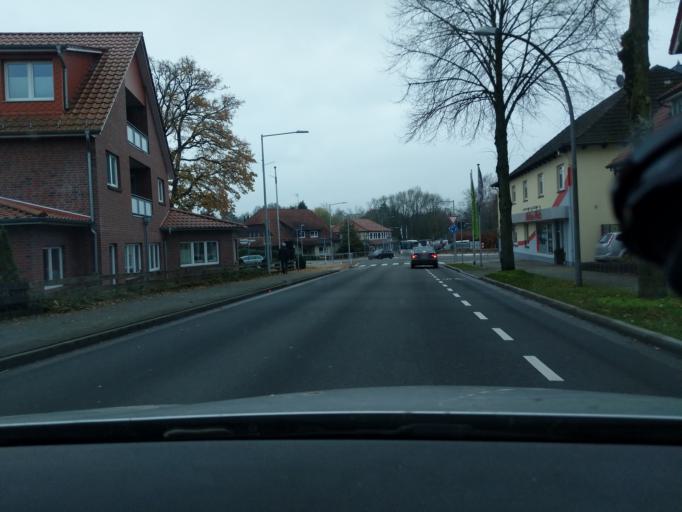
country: DE
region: Lower Saxony
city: Heeslingen
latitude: 53.3155
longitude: 9.3353
